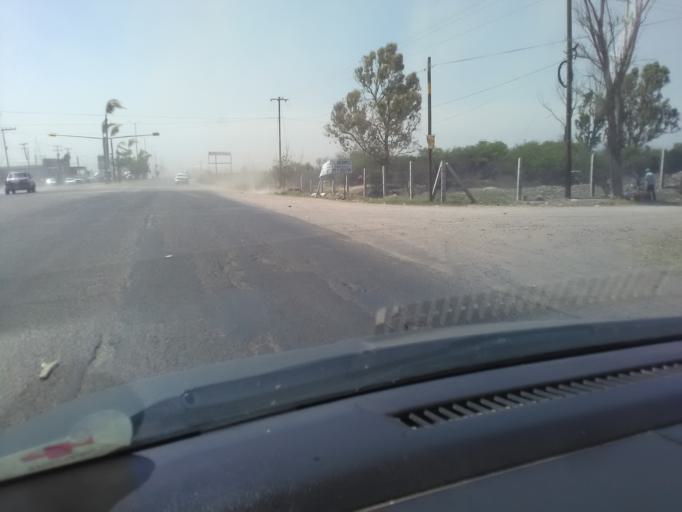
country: MX
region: Durango
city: Victoria de Durango
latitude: 24.0282
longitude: -104.5916
